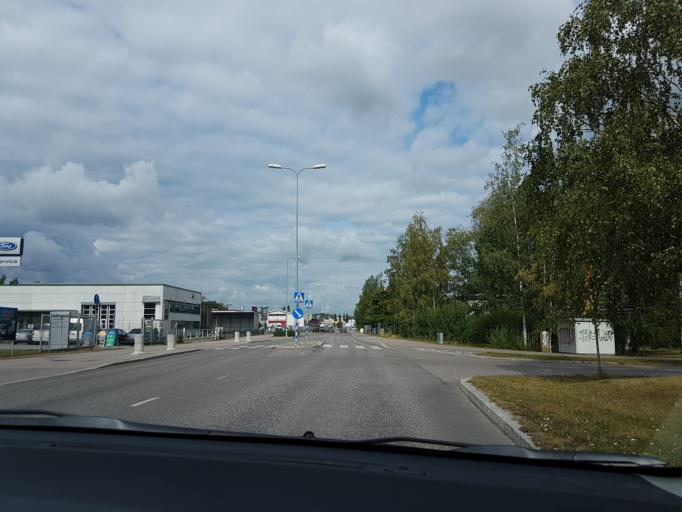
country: FI
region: Uusimaa
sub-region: Helsinki
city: Jaervenpaeae
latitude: 60.4722
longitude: 25.1162
